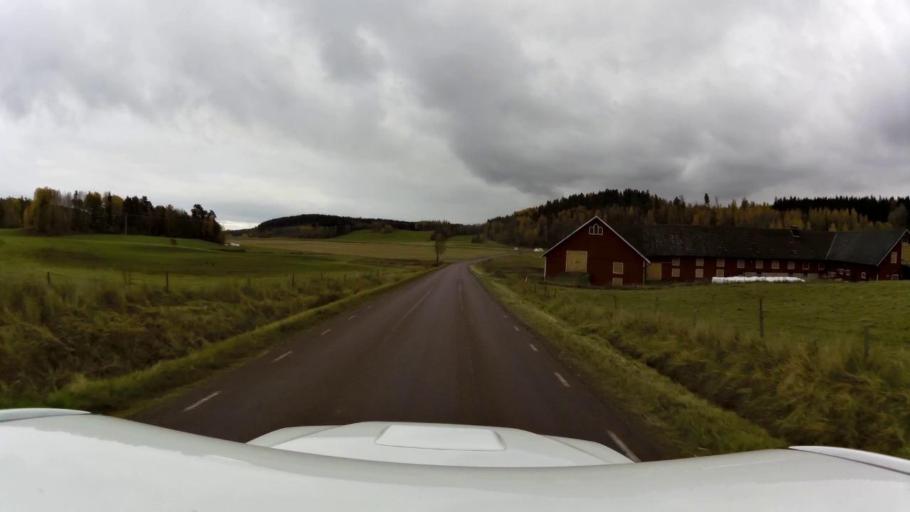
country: SE
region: OEstergoetland
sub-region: Linkopings Kommun
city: Ljungsbro
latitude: 58.5566
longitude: 15.5201
